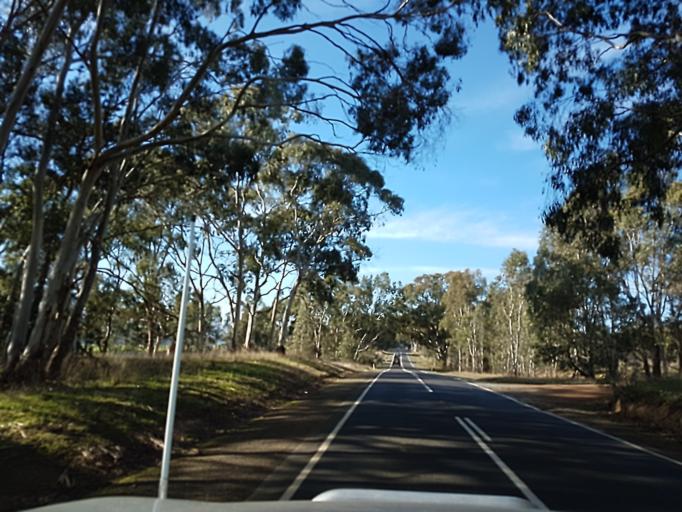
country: AU
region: Victoria
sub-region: Murrindindi
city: Alexandra
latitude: -37.1485
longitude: 145.6082
